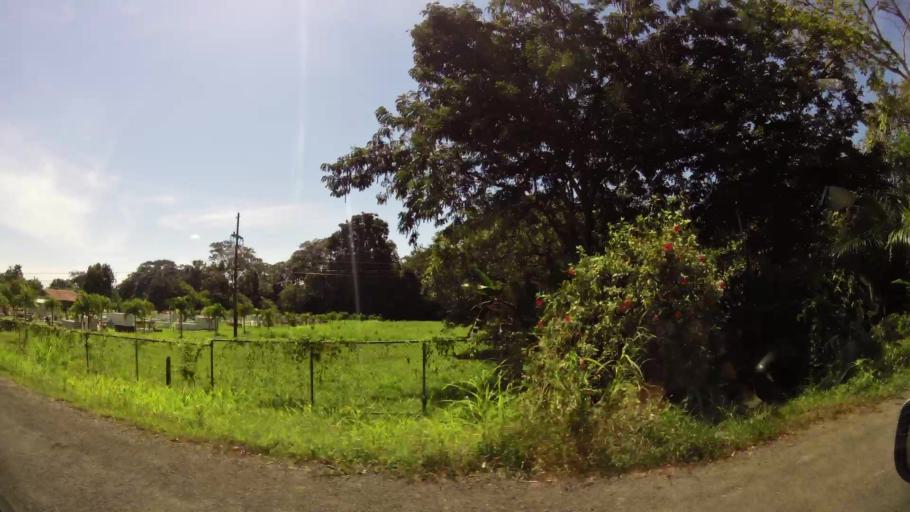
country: CR
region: Puntarenas
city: Quepos
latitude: 9.3290
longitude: -83.9543
